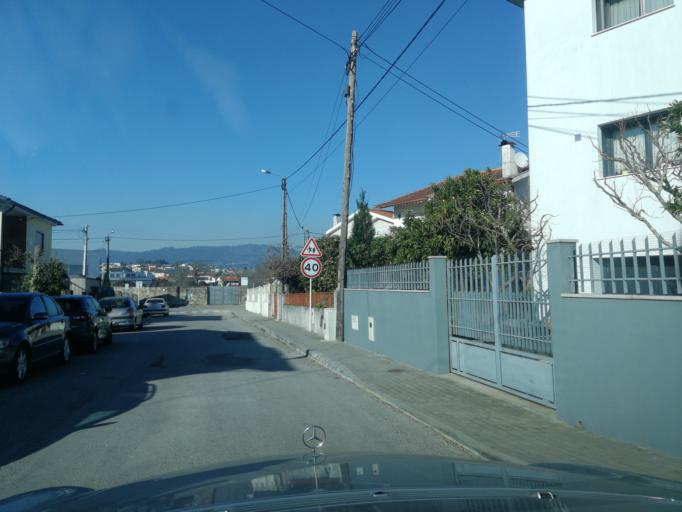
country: PT
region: Braga
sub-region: Guimaraes
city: Ponte
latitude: 41.4892
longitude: -8.3414
